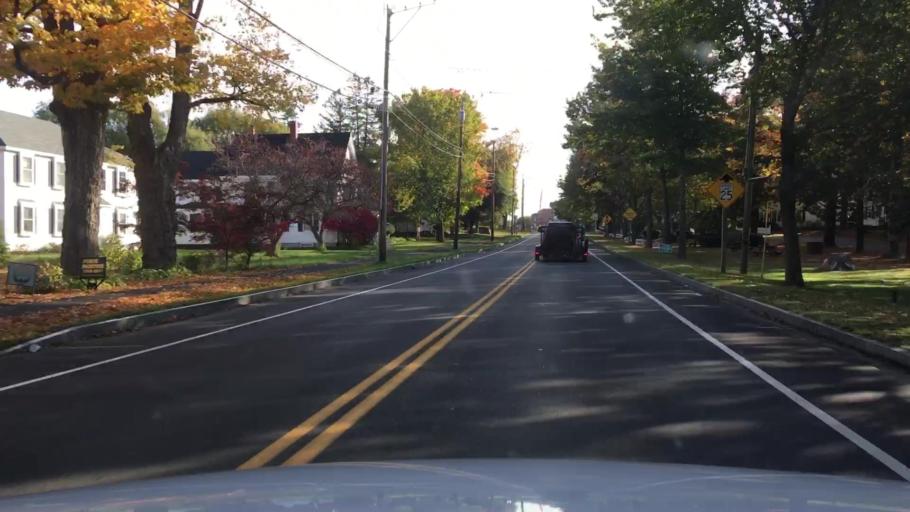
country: US
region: Maine
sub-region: Knox County
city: Thomaston
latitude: 44.0782
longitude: -69.1877
